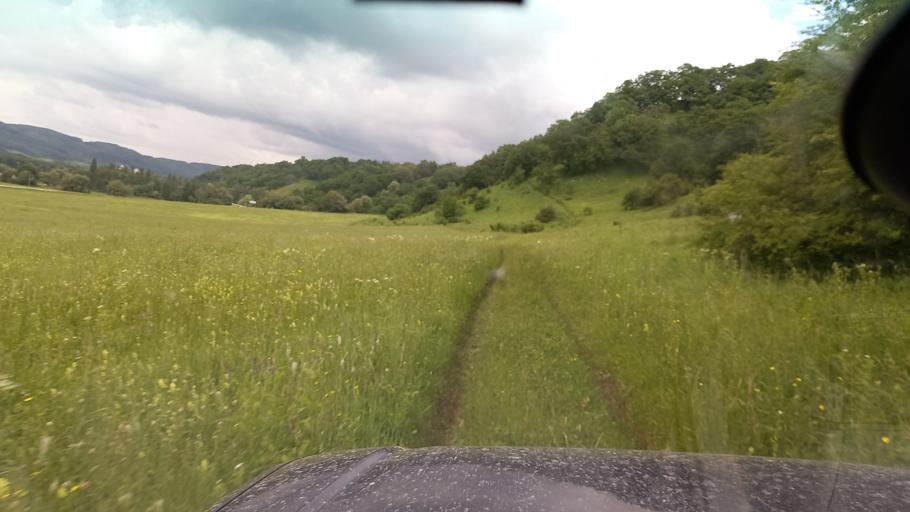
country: RU
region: Krasnodarskiy
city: Psebay
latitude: 44.1503
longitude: 40.8573
